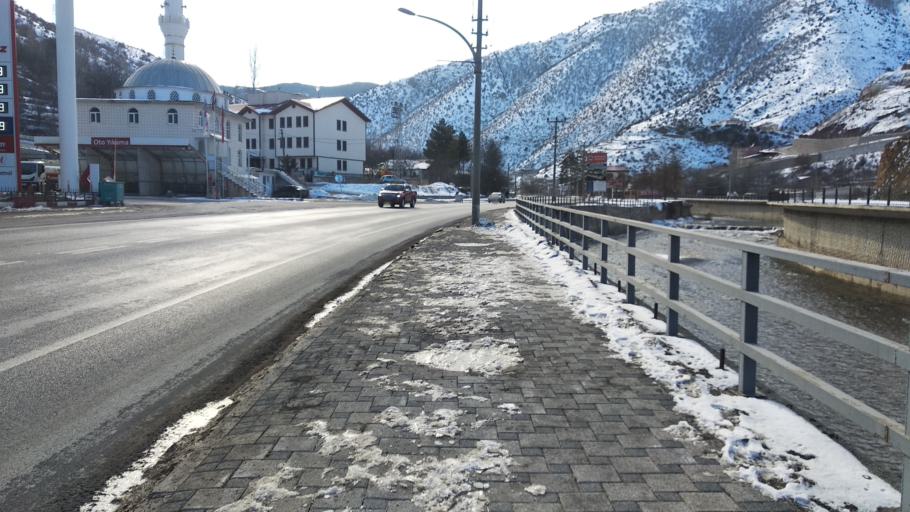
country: TR
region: Gumushane
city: Gumushkhane
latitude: 40.4451
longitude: 39.5038
